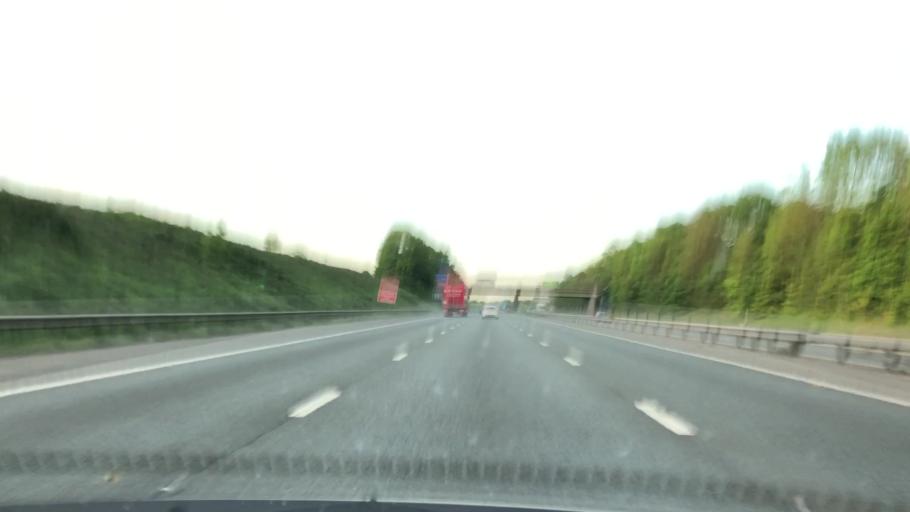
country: GB
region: England
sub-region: Cheshire West and Chester
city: Elton
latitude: 53.2573
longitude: -2.8284
